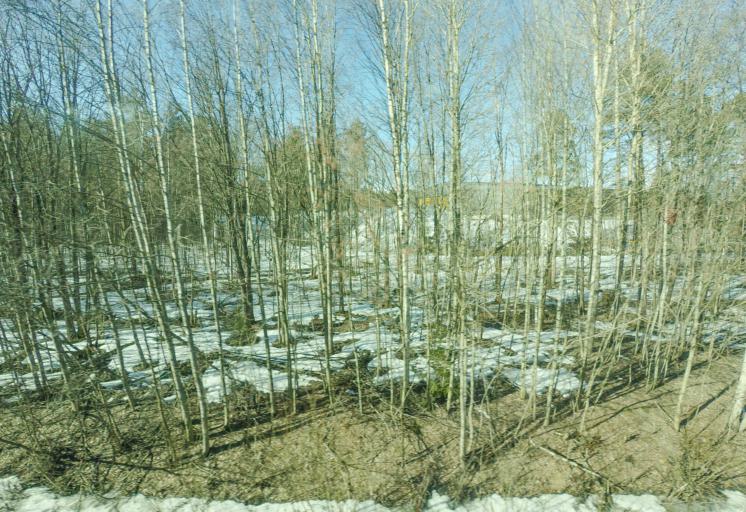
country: FI
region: South Karelia
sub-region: Lappeenranta
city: Lappeenranta
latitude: 61.0545
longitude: 28.2236
